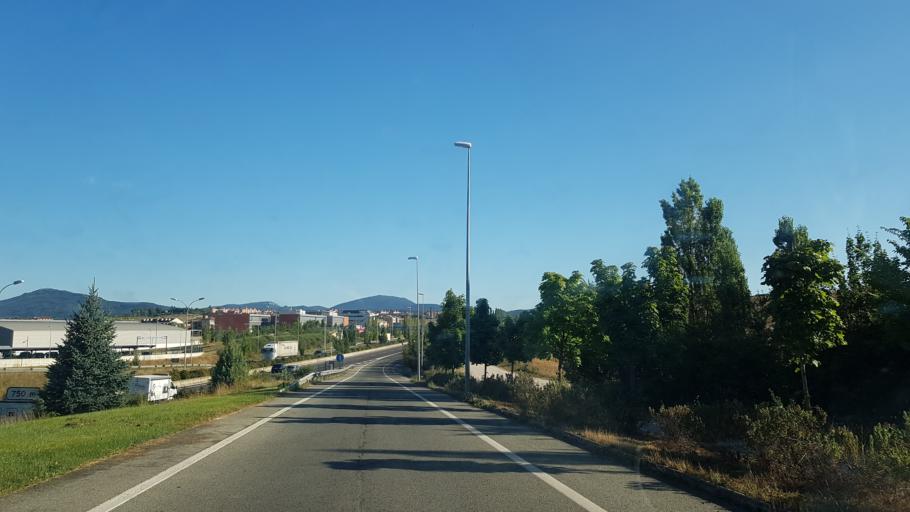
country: ES
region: Navarre
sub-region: Provincia de Navarra
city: Burlata
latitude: 42.7932
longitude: -1.6120
